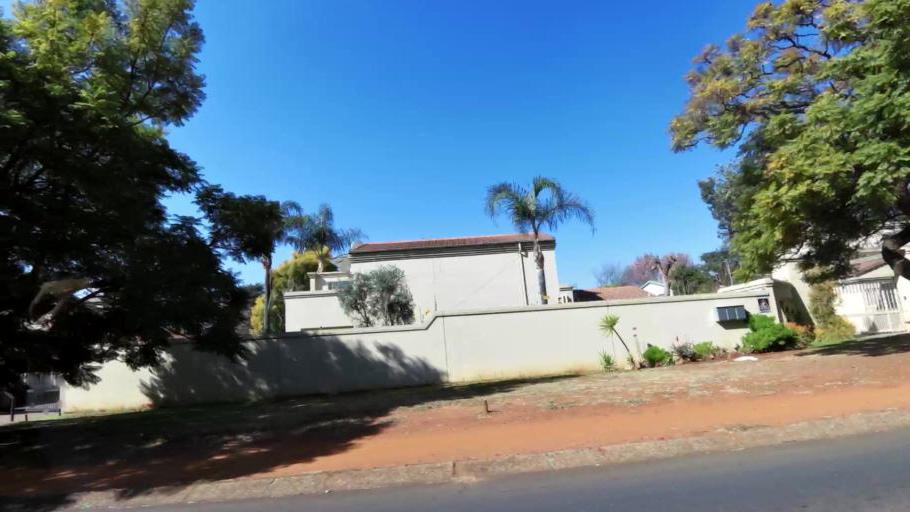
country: ZA
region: Gauteng
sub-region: City of Johannesburg Metropolitan Municipality
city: Roodepoort
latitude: -26.1258
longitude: 27.9479
